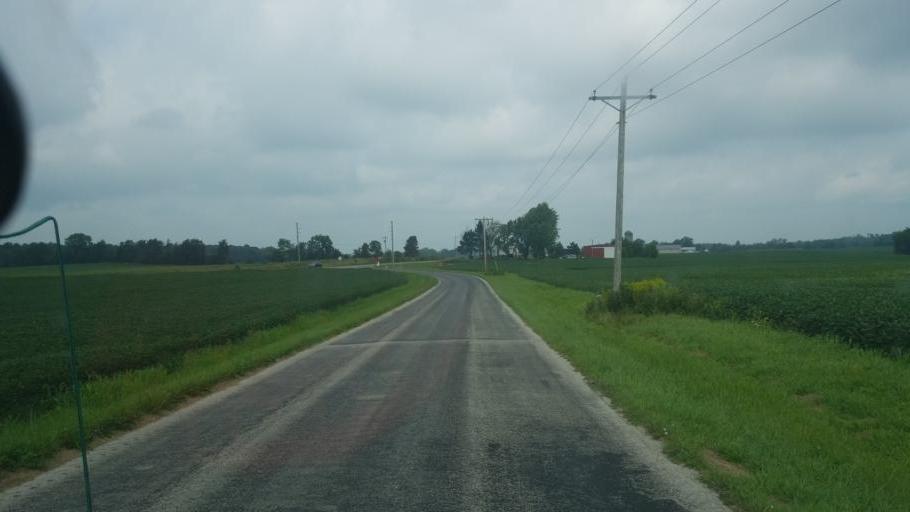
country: US
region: Ohio
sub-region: Huron County
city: Greenwich
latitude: 40.9988
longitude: -82.4826
